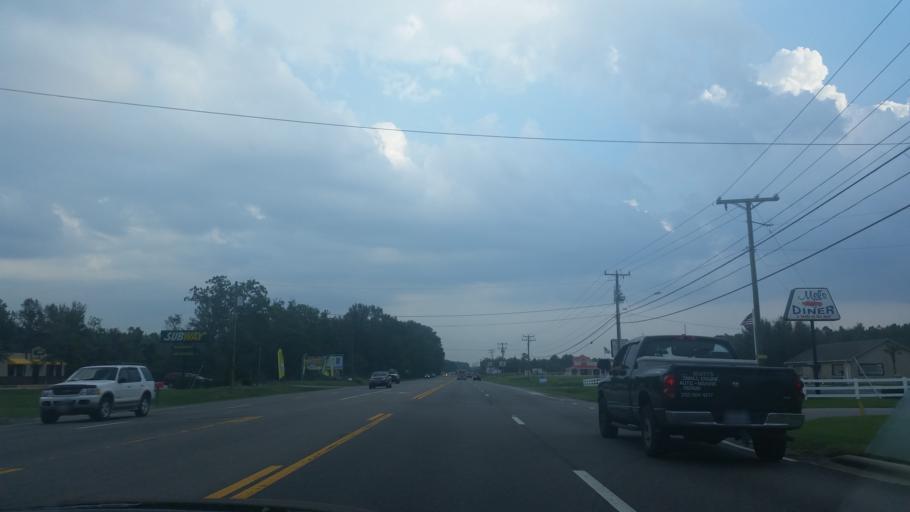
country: US
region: North Carolina
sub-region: Dare County
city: Southern Shores
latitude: 36.2285
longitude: -75.8728
